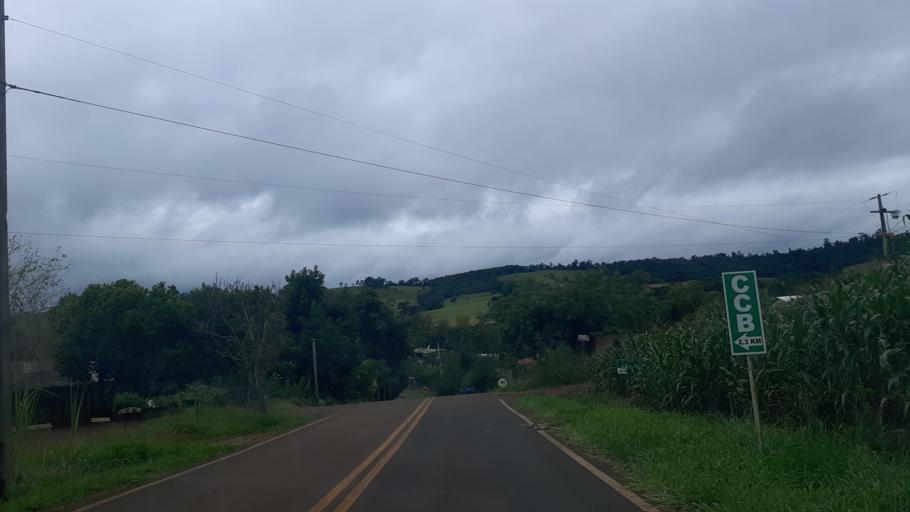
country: BR
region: Parana
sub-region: Ampere
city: Ampere
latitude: -25.9743
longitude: -53.4439
